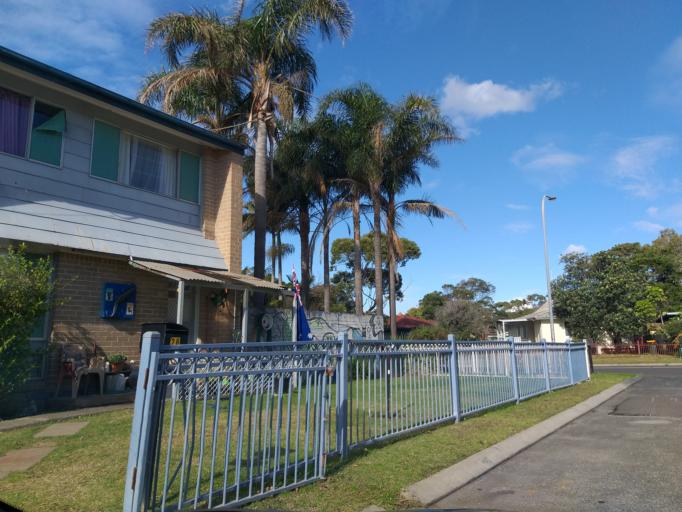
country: AU
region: New South Wales
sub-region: Wollongong
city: East Corrimal
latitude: -34.3661
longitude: 150.9216
